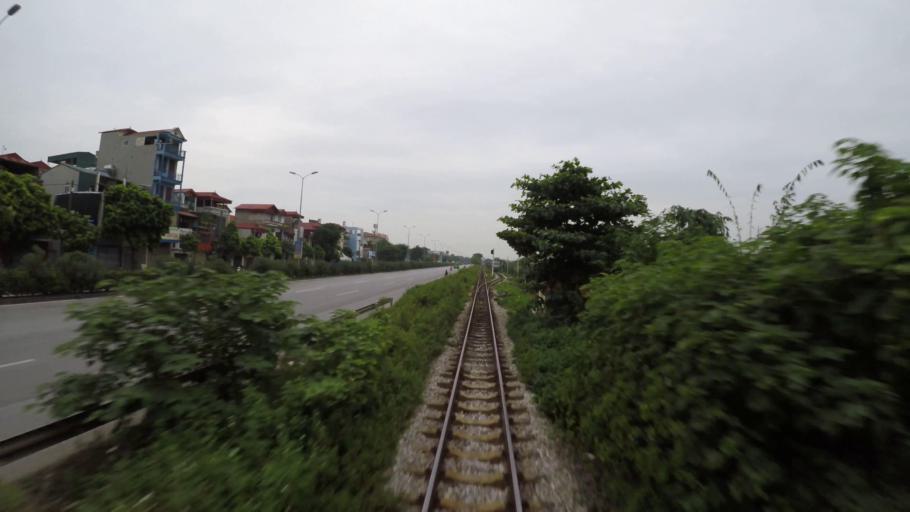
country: VN
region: Hung Yen
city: Nhu Quynh
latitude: 21.0010
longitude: 105.9657
